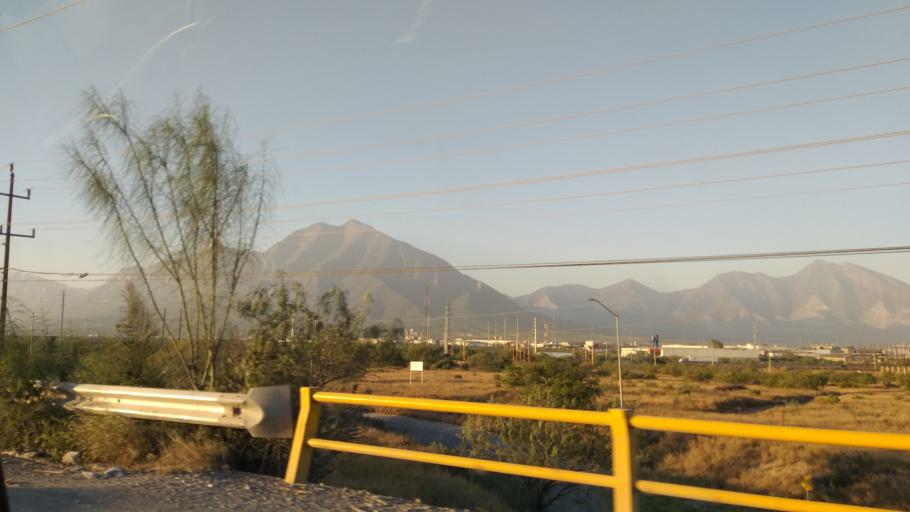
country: MX
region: Nuevo Leon
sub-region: Garcia
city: Parque Industrial Ciudad Mitras
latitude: 25.7779
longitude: -100.4446
